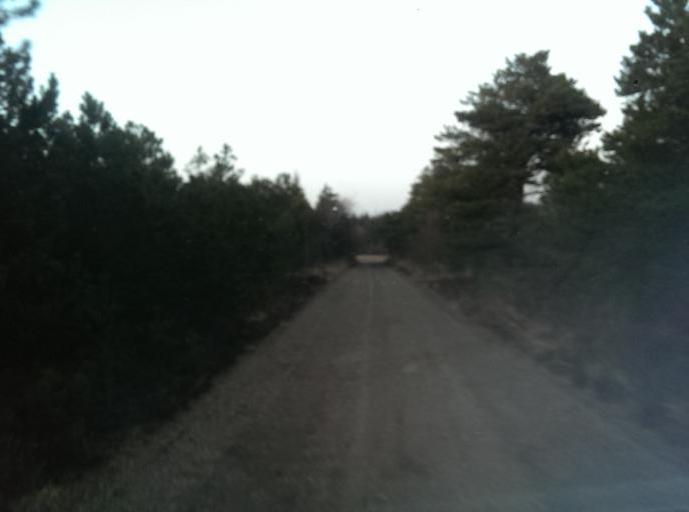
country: DK
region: South Denmark
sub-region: Varde Kommune
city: Oksbol
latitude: 55.5538
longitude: 8.3197
